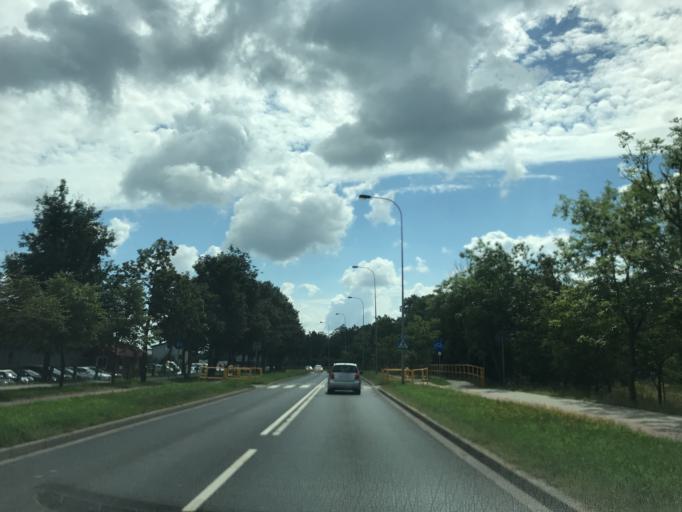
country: PL
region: Warmian-Masurian Voivodeship
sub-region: Powiat ostrodzki
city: Ostroda
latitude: 53.6873
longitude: 19.9865
